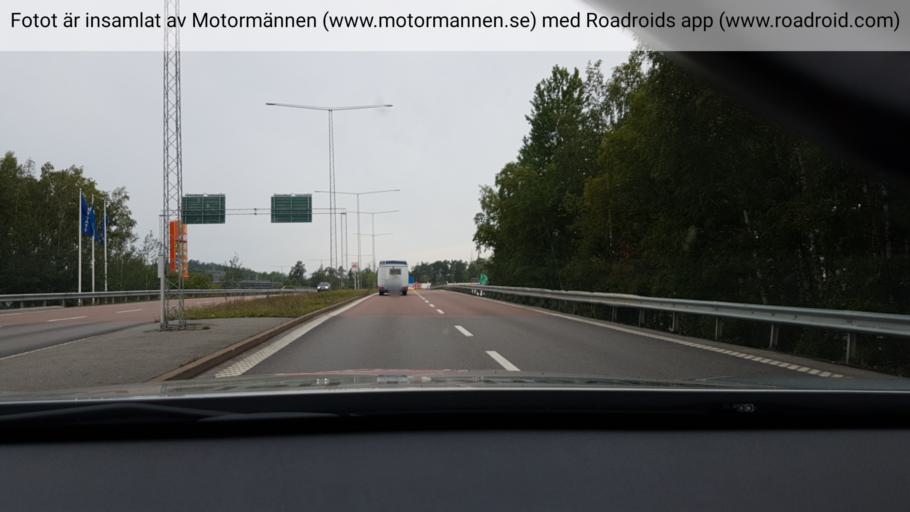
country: SE
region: Stockholm
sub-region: Botkyrka Kommun
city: Fittja
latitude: 59.2506
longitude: 17.8586
